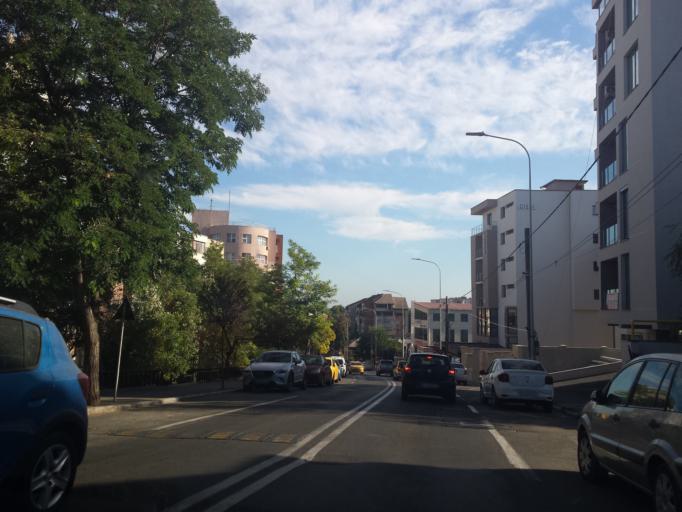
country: RO
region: Tulcea
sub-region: Municipiul Tulcea
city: Tulcea
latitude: 45.1702
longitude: 28.7974
